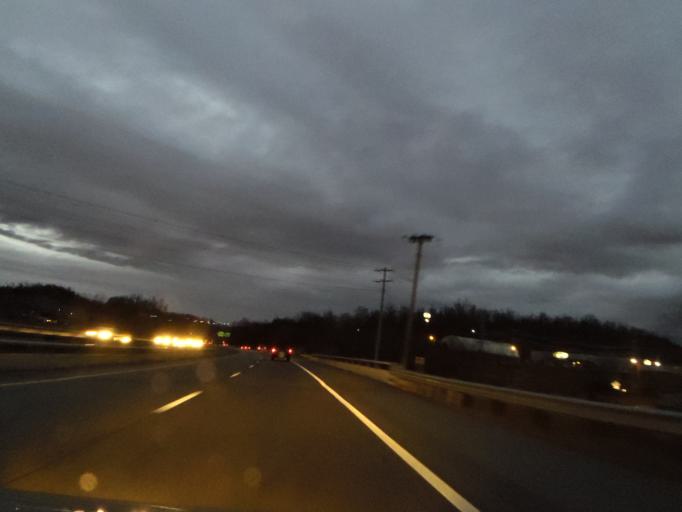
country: US
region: Tennessee
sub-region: Sullivan County
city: Colonial Heights
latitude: 36.4472
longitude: -82.5208
